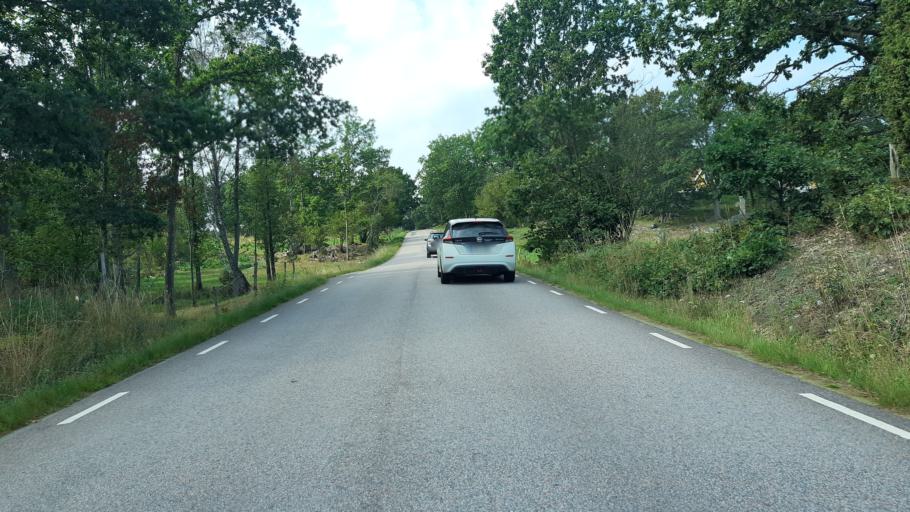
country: SE
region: Blekinge
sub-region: Karlskrona Kommun
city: Nattraby
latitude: 56.1883
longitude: 15.5209
